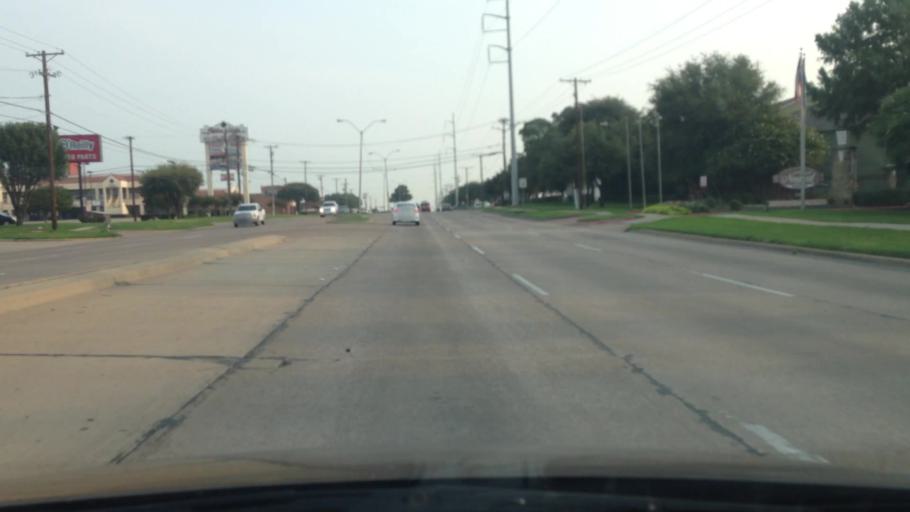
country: US
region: Texas
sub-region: Dallas County
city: Irving
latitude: 32.8521
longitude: -96.9922
